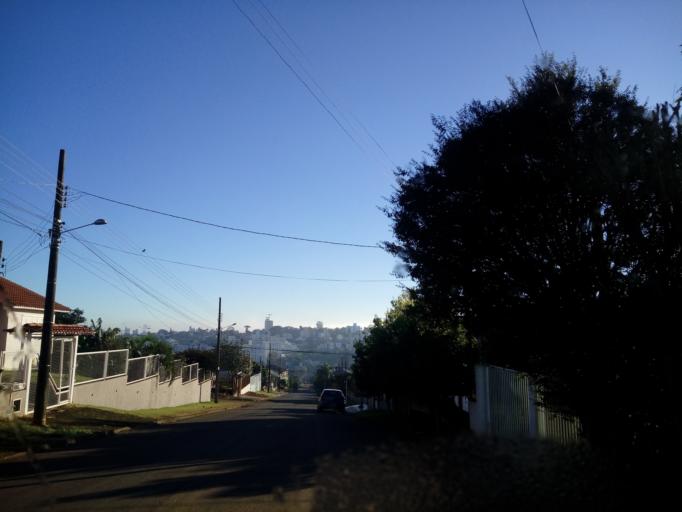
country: BR
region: Santa Catarina
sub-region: Chapeco
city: Chapeco
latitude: -27.1200
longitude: -52.6211
